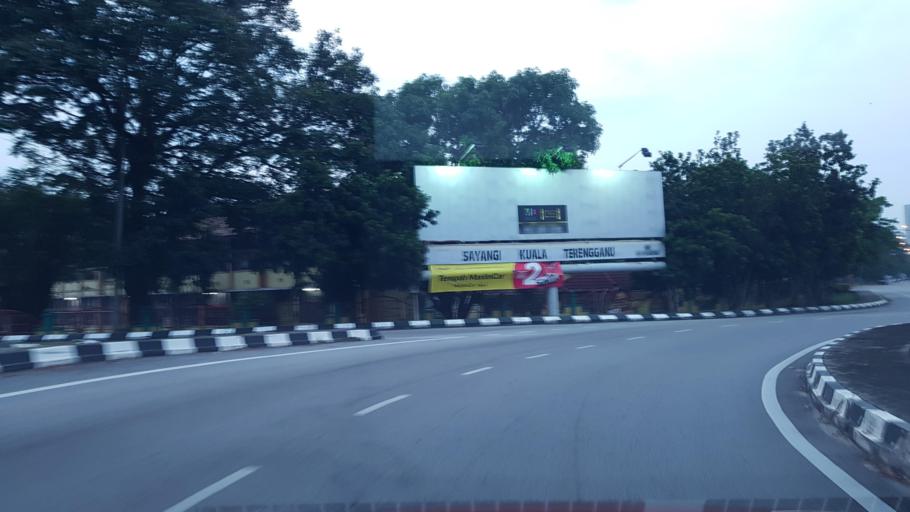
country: MY
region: Terengganu
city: Kuala Terengganu
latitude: 5.3204
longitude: 103.1421
